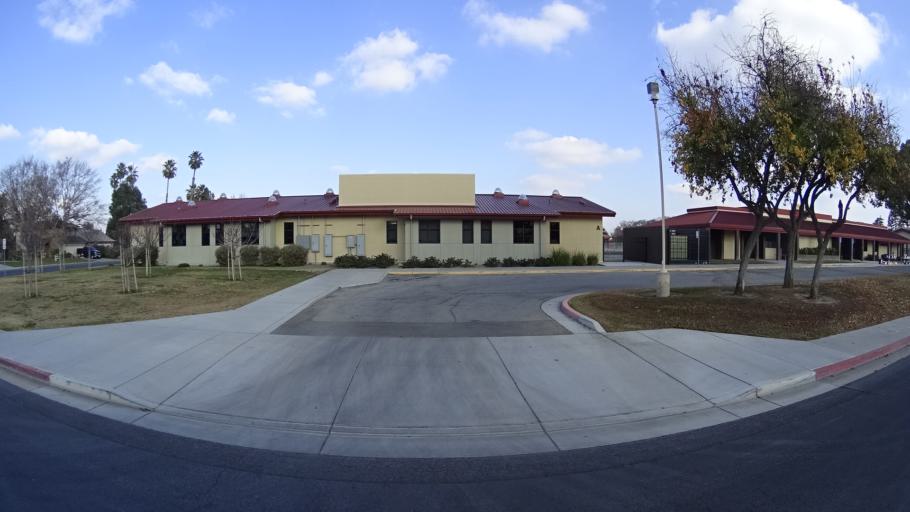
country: US
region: California
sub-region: Kern County
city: Greenacres
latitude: 35.3137
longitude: -119.1042
